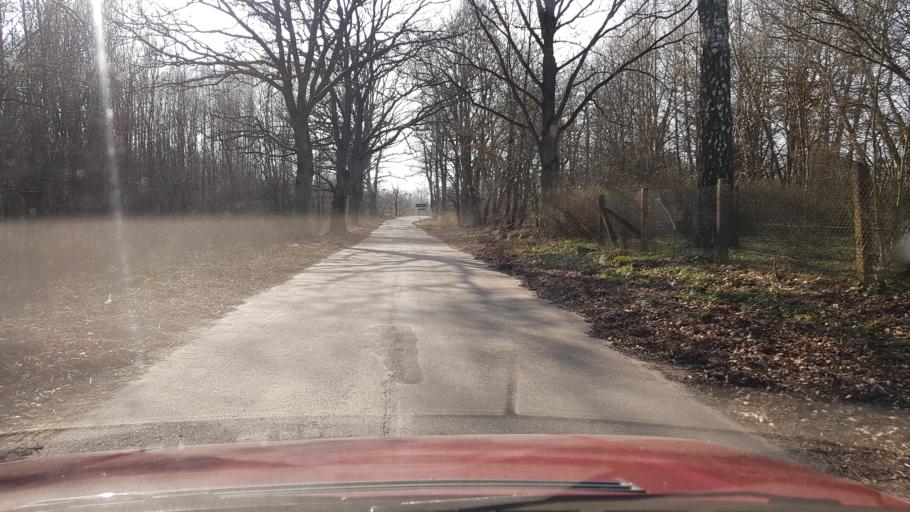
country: PL
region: West Pomeranian Voivodeship
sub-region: Powiat gryficki
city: Ploty
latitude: 53.8296
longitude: 15.3327
